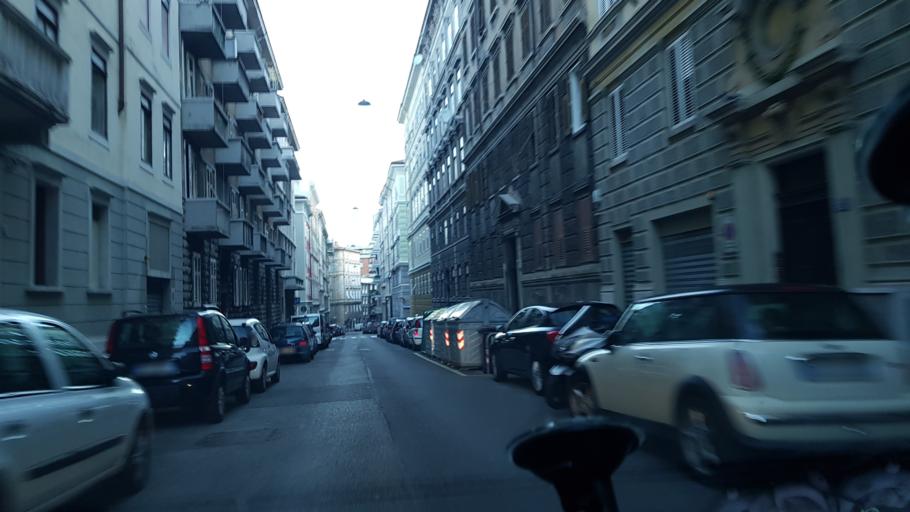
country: IT
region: Friuli Venezia Giulia
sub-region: Provincia di Trieste
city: Trieste
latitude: 45.6481
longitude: 13.7861
